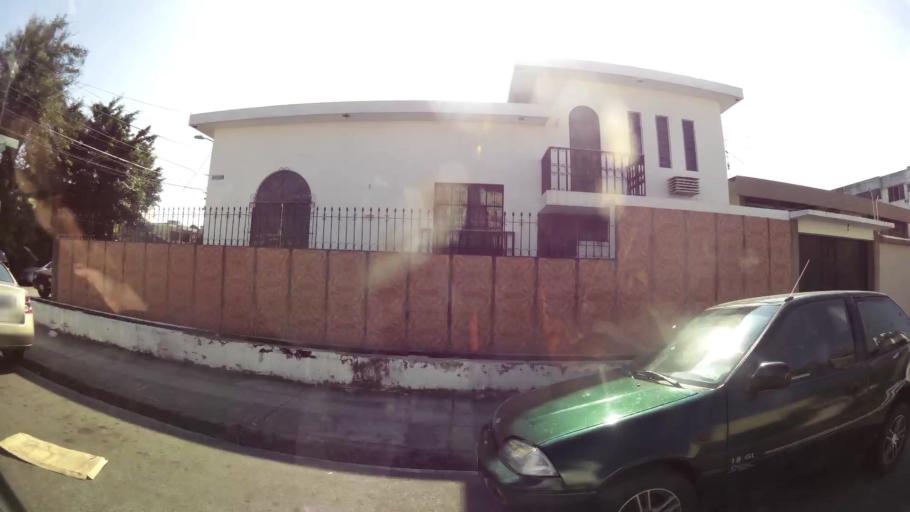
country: EC
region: Guayas
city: Guayaquil
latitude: -2.1707
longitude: -79.9067
